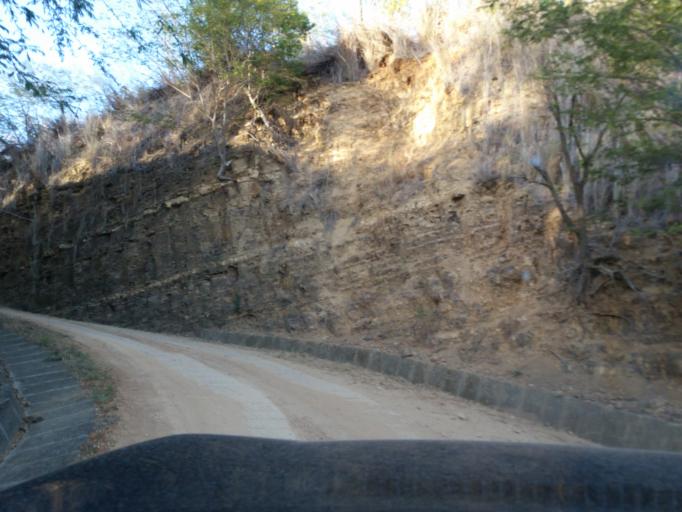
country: NI
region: Rivas
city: San Juan del Sur
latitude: 11.1805
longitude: -85.8115
